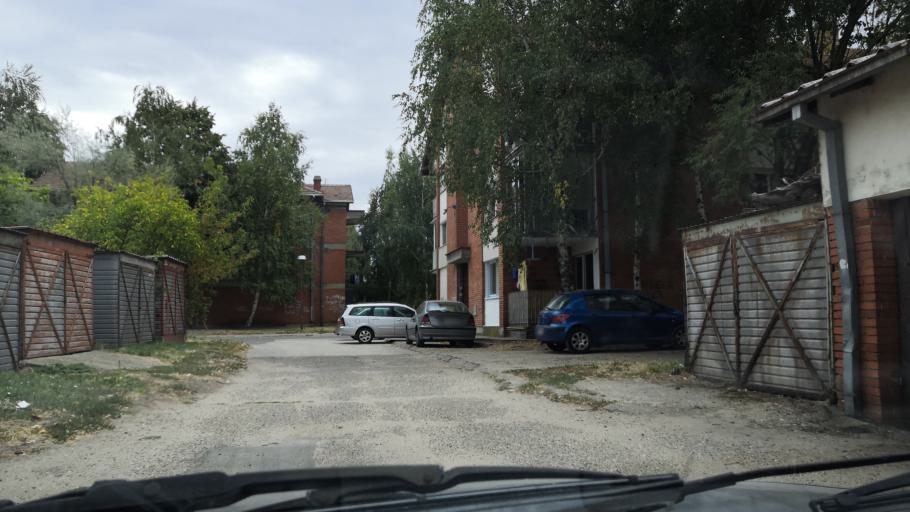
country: RS
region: Central Serbia
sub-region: Borski Okrug
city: Negotin
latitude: 44.2277
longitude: 22.5195
